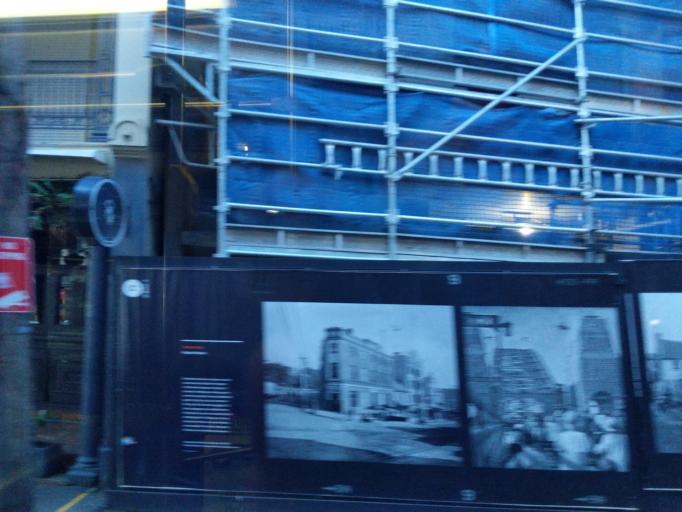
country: AU
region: New South Wales
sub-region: City of Sydney
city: Darlinghurst
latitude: -33.8769
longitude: 151.2211
